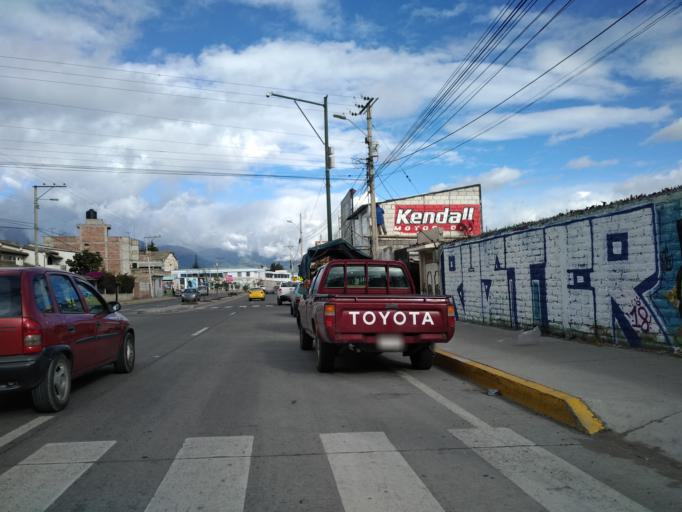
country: EC
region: Chimborazo
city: Riobamba
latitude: -1.6714
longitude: -78.6637
